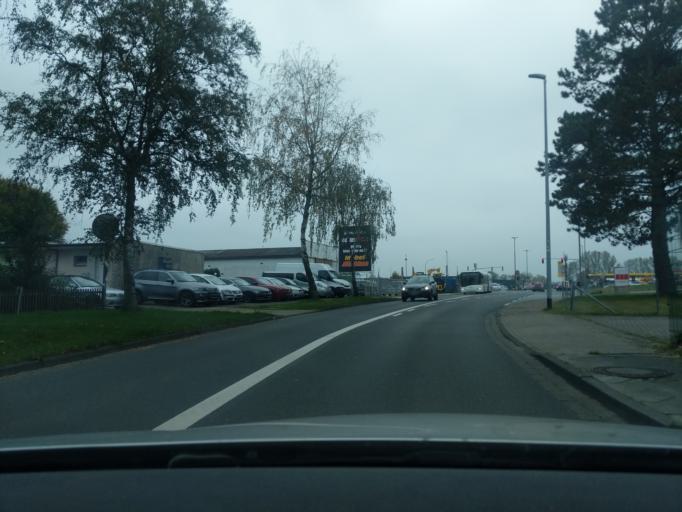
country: DE
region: Lower Saxony
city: Stade
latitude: 53.5960
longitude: 9.4231
